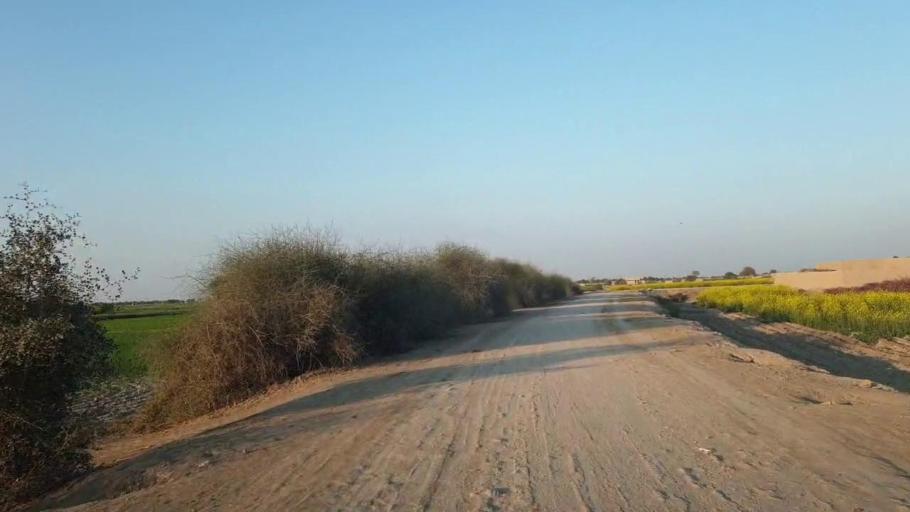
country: PK
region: Sindh
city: Shahpur Chakar
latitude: 26.1527
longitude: 68.5652
